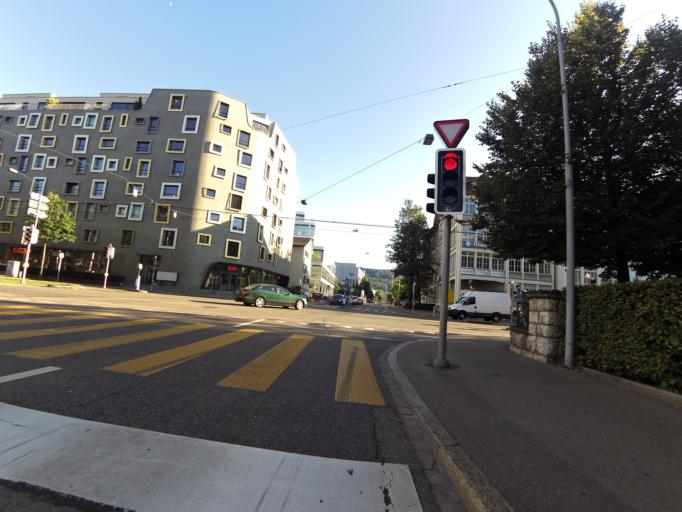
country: CH
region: Zurich
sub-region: Bezirk Zuerich
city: Zuerich (Kreis 9) / Altstetten
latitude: 47.3852
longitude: 8.4955
